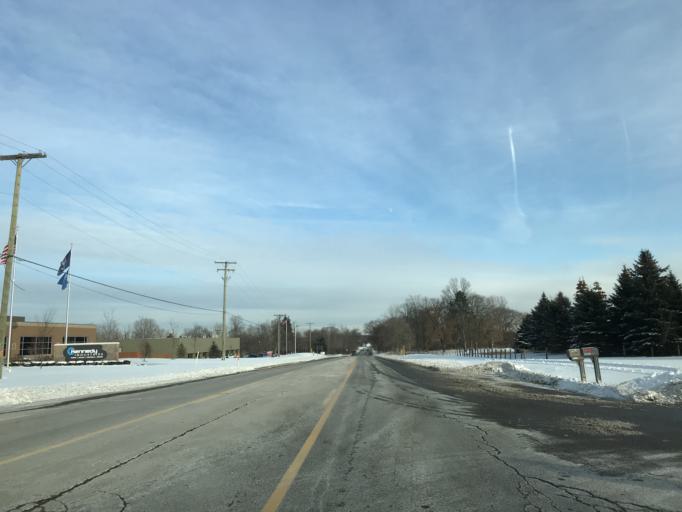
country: US
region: Michigan
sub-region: Oakland County
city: Wixom
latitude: 42.5236
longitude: -83.5650
